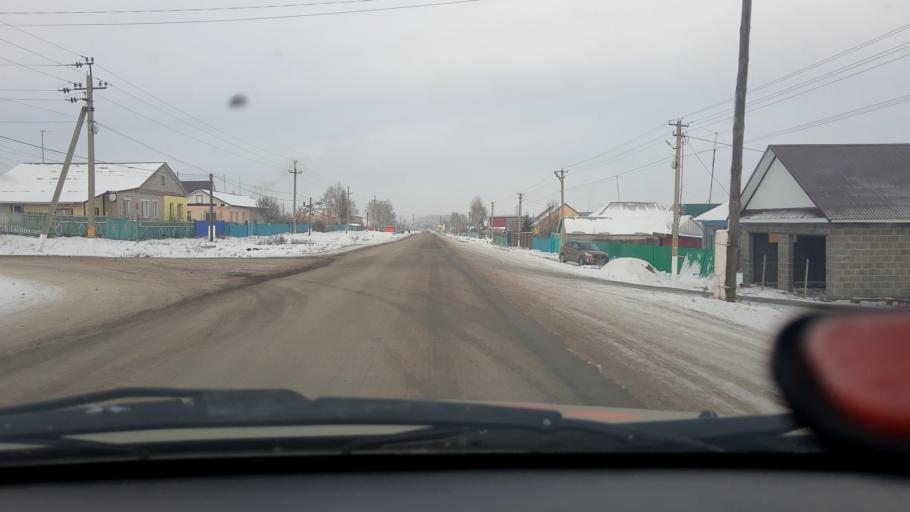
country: RU
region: Bashkortostan
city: Avdon
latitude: 54.4142
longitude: 55.8078
